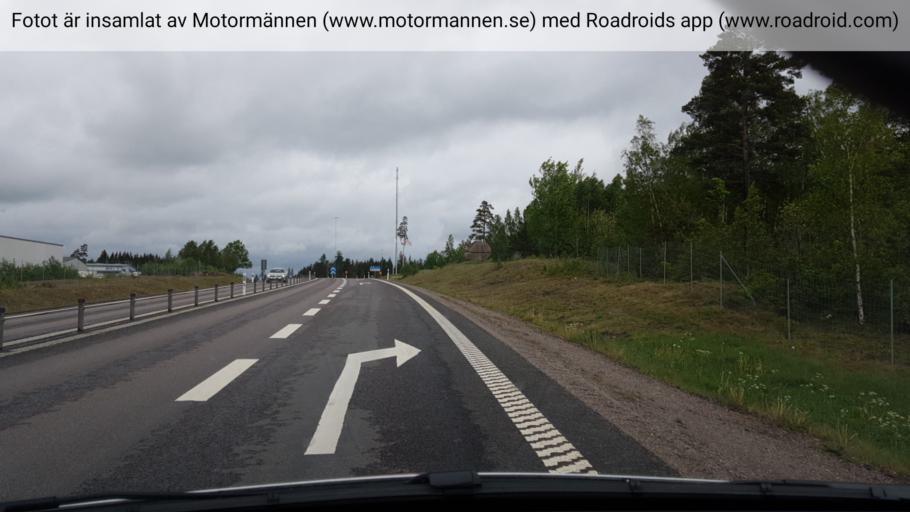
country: SE
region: Joenkoeping
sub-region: Tranas Kommun
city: Tranas
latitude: 58.0299
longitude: 14.9515
